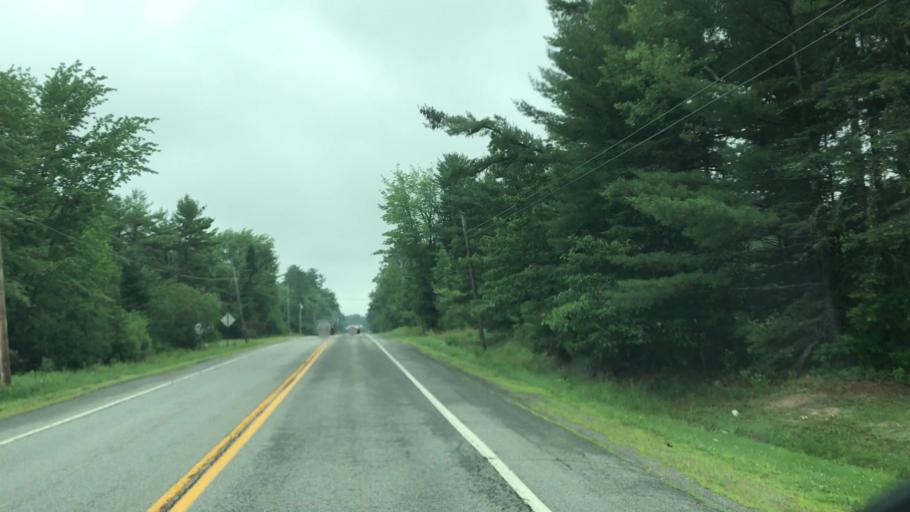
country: US
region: Maine
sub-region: Penobscot County
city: Howland
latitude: 45.2891
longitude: -68.6235
